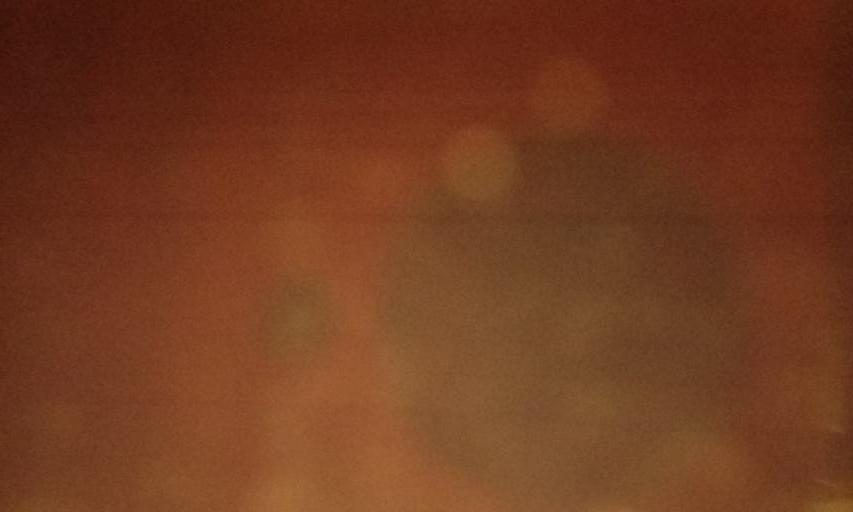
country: JP
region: Osaka
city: Suita
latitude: 34.7652
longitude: 135.5090
